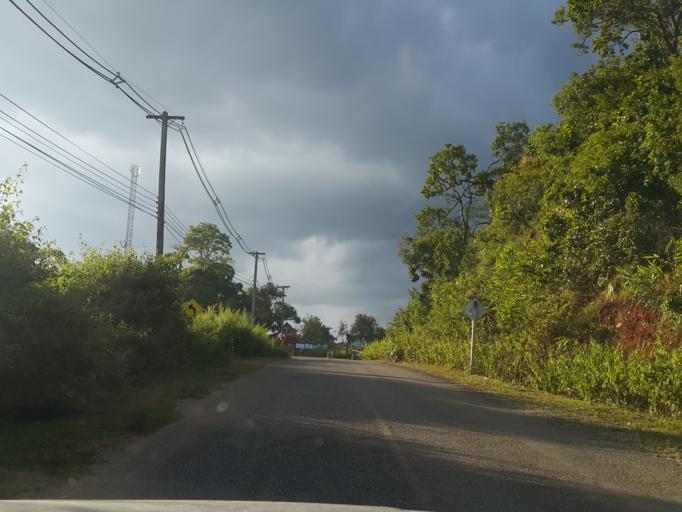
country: TH
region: Chiang Mai
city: Mae Chaem
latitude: 18.7451
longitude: 98.2162
